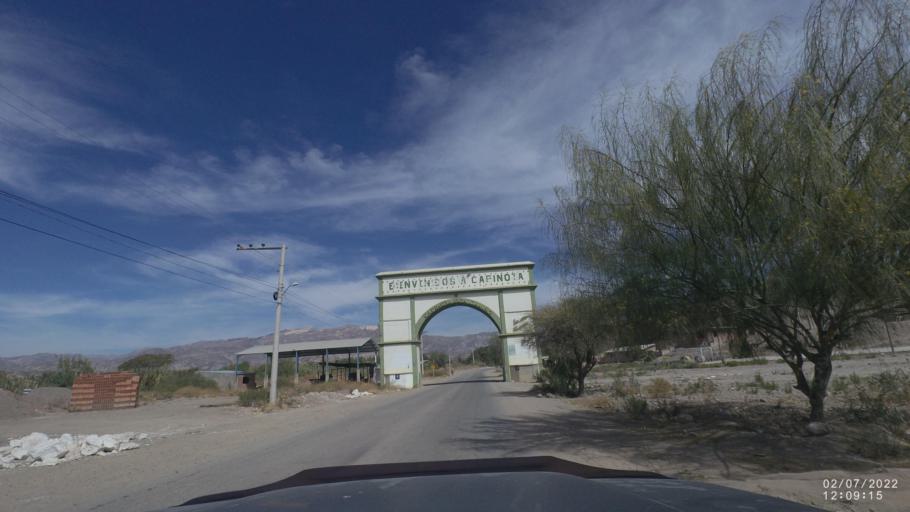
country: BO
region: Cochabamba
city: Capinota
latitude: -17.6930
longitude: -66.2582
